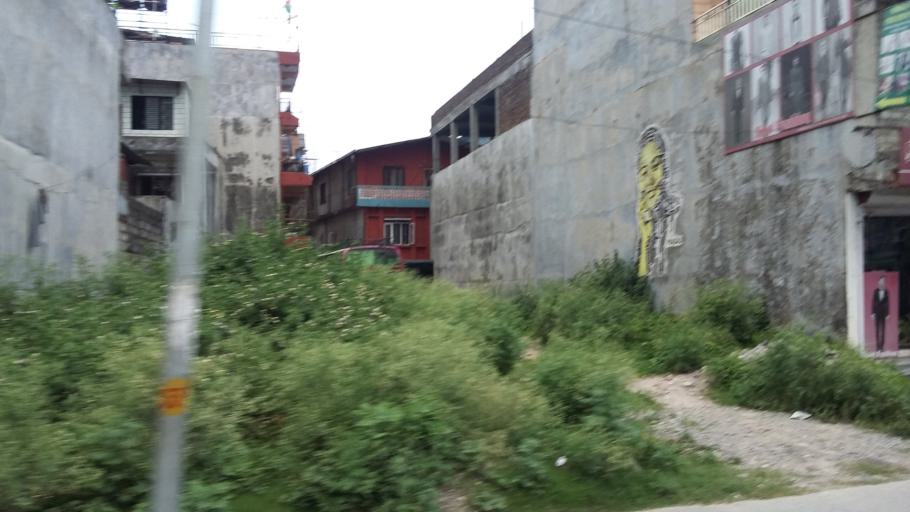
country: NP
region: Western Region
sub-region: Gandaki Zone
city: Pokhara
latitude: 28.2159
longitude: 83.9862
